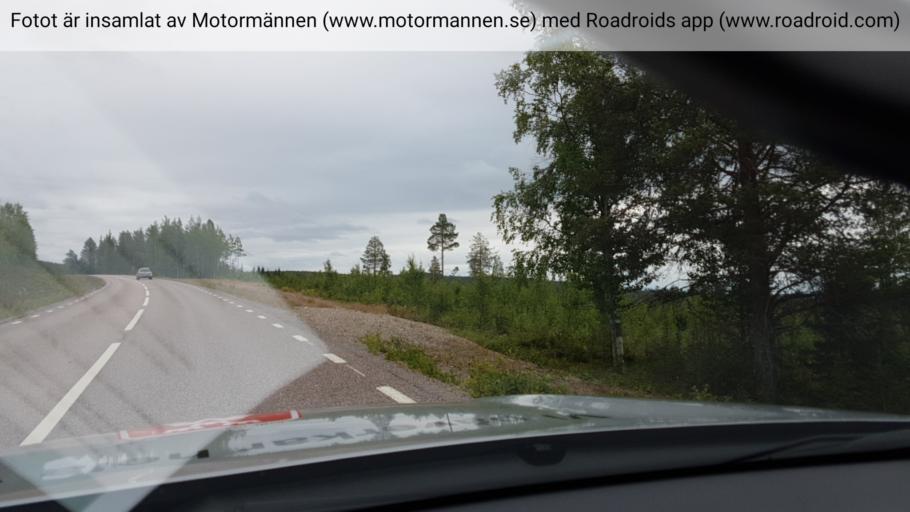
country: SE
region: Norrbotten
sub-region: Gallivare Kommun
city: Gaellivare
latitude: 67.0461
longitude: 21.6198
